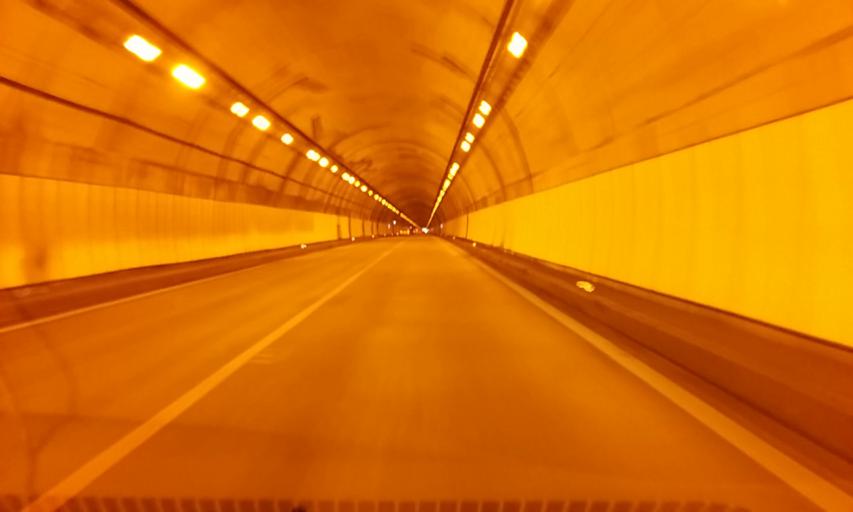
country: JP
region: Kyoto
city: Fukuchiyama
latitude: 35.2200
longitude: 135.1795
